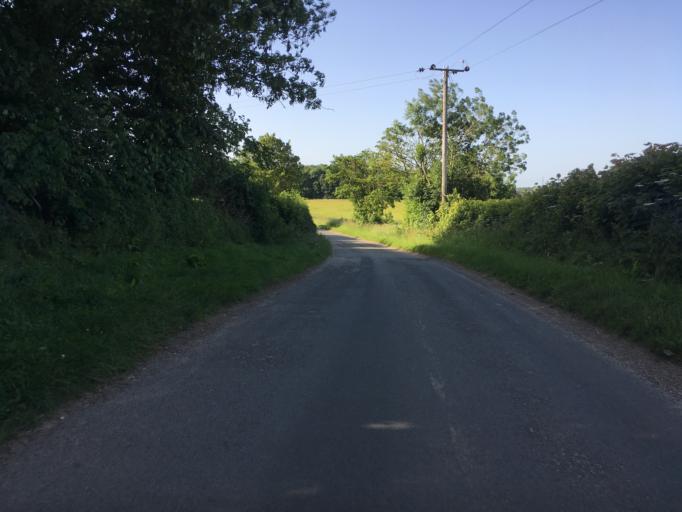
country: GB
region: England
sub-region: Gloucestershire
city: Lechlade
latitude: 51.7535
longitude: -1.7214
